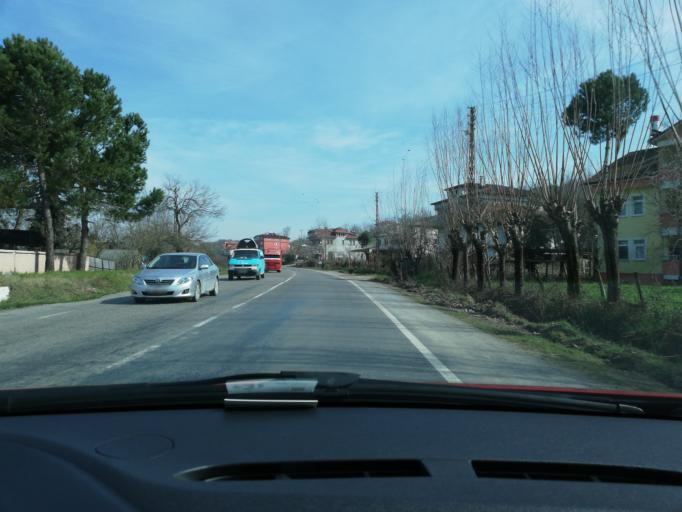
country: TR
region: Bartin
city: Kozcagiz
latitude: 41.4930
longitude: 32.3478
